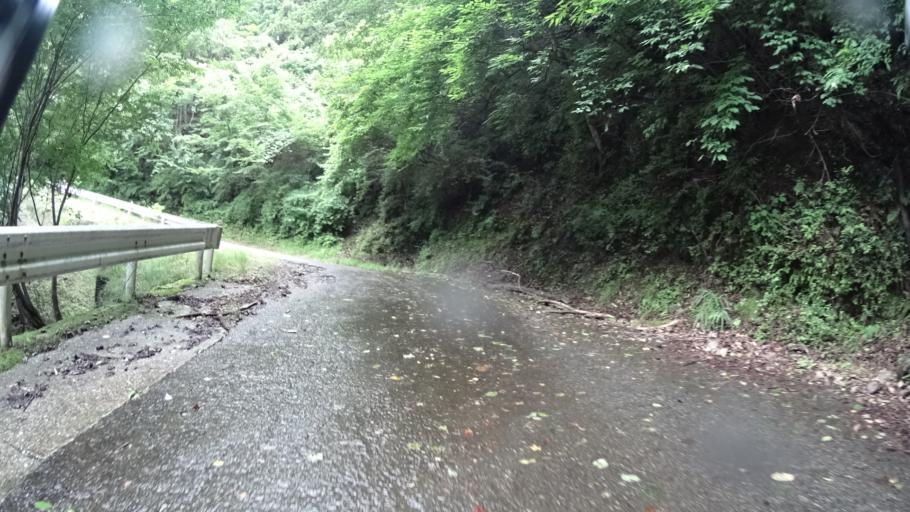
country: JP
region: Saitama
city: Chichibu
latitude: 35.8951
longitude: 139.1281
